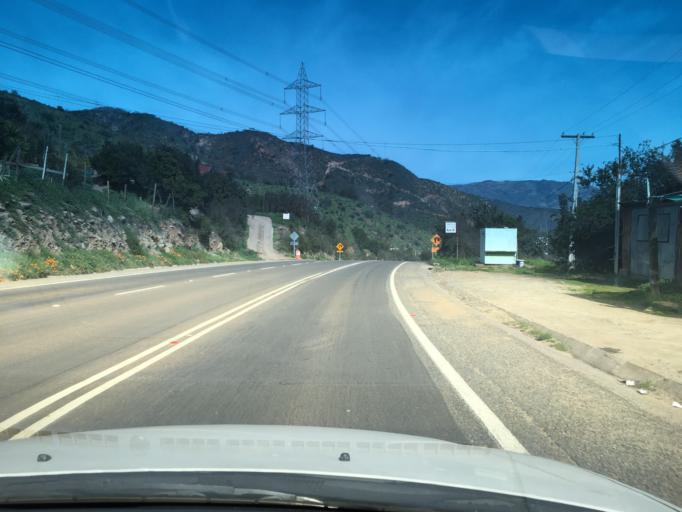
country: CL
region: Valparaiso
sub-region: Provincia de Marga Marga
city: Limache
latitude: -33.0590
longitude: -71.0472
